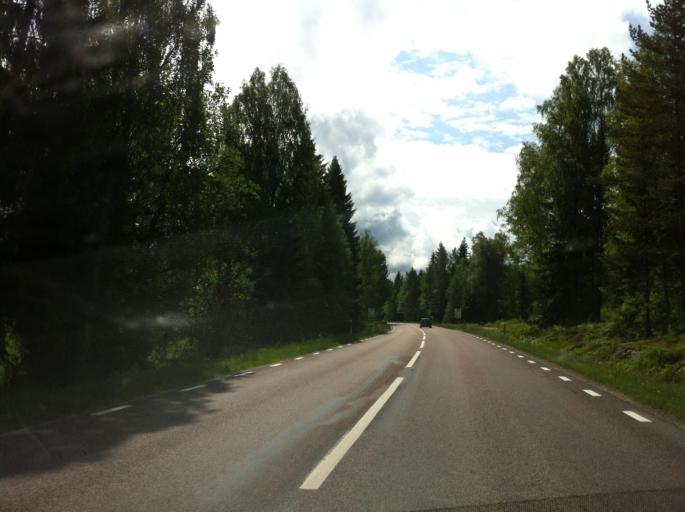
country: SE
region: Vaermland
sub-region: Karlstads Kommun
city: Edsvalla
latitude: 59.5480
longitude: 13.1955
